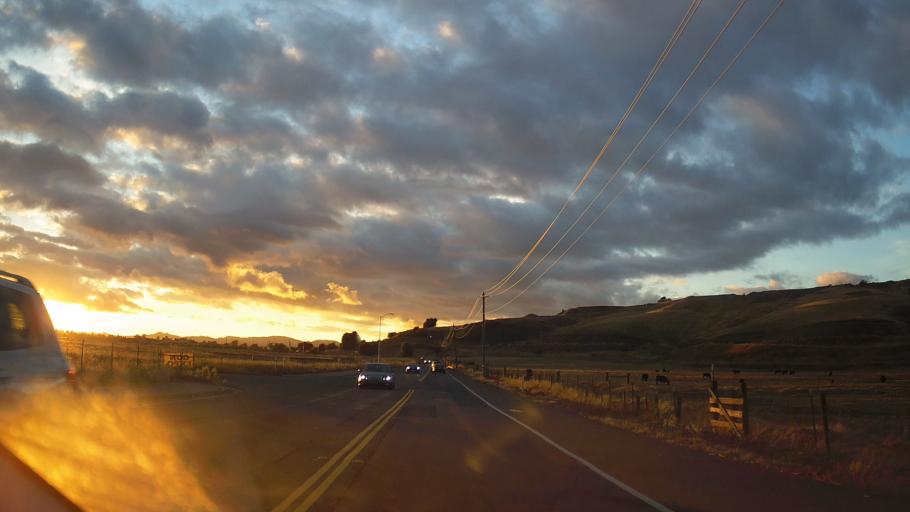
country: US
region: California
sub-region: Solano County
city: Fairfield
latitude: 38.2872
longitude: -121.9888
